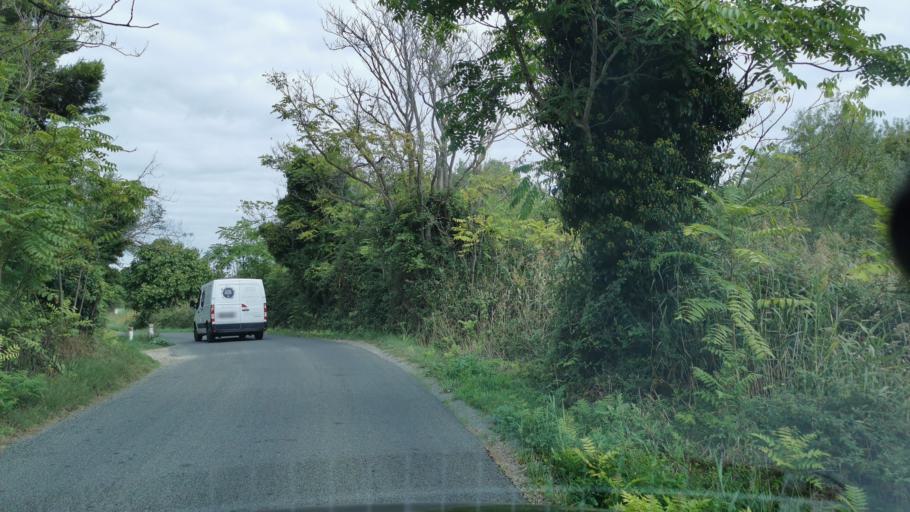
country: FR
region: Languedoc-Roussillon
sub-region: Departement de l'Herault
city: Vendres
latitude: 43.2236
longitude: 3.1943
